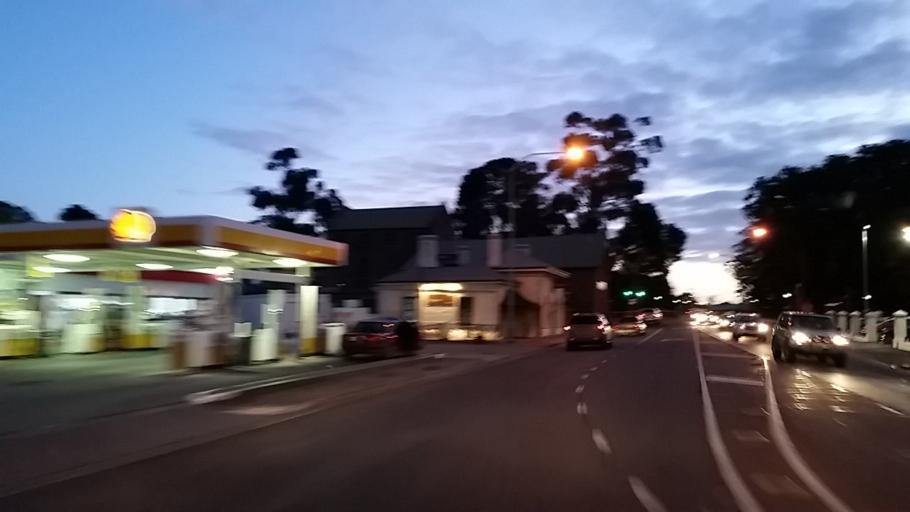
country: AU
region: South Australia
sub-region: Gawler
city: Gawler
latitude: -34.6028
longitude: 138.7492
